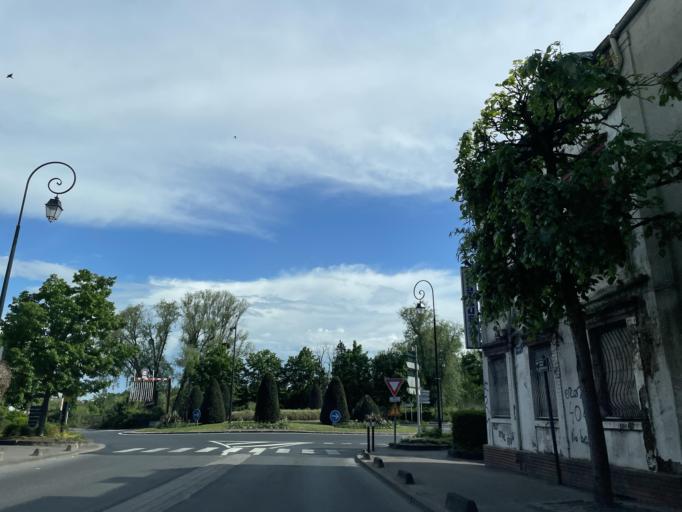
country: FR
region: Ile-de-France
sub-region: Departement du Val-d'Oise
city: Arnouville
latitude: 48.9771
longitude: 2.4229
